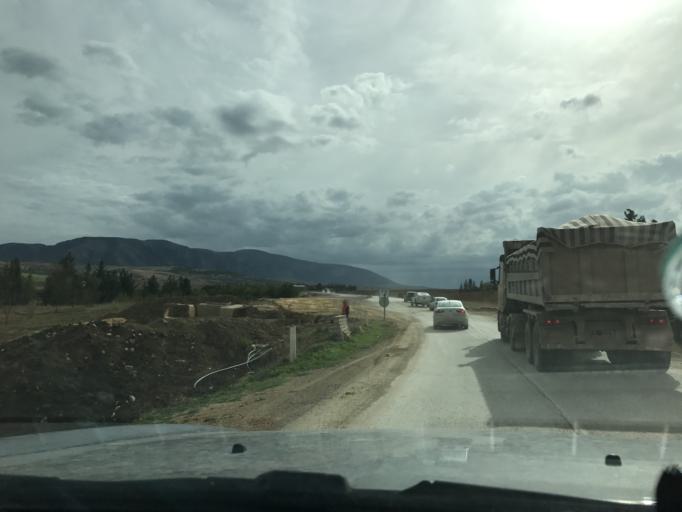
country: TN
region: Silyanah
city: Bu `Aradah
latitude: 36.1506
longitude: 9.6330
